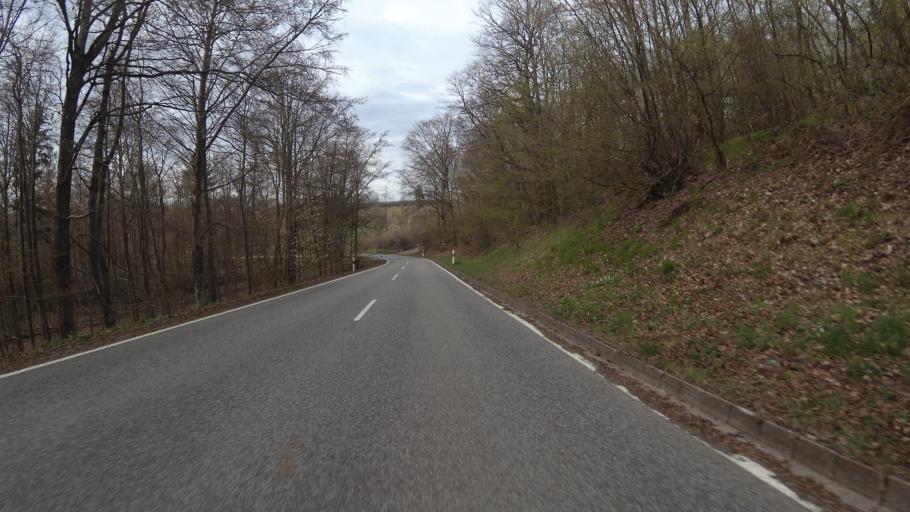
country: DE
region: Rheinland-Pfalz
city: Herschweiler-Pettersheim
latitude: 49.4825
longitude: 7.3615
